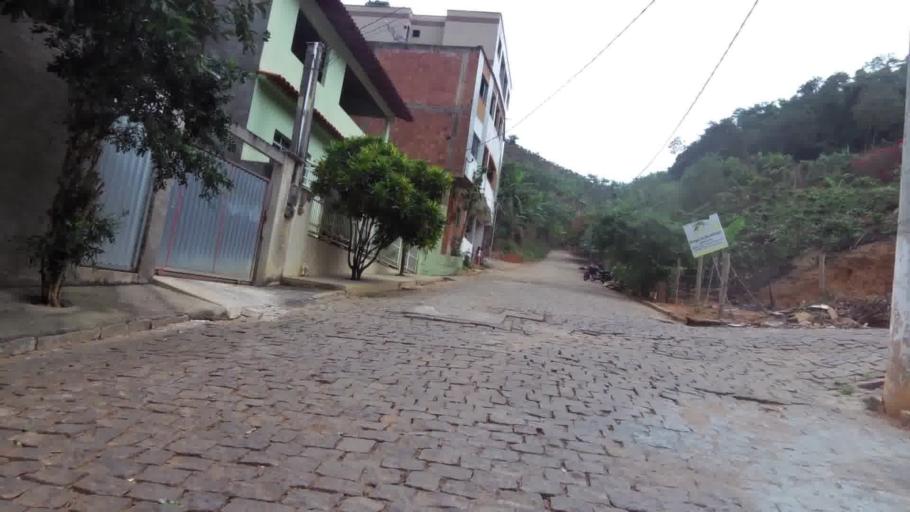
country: BR
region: Espirito Santo
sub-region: Alfredo Chaves
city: Alfredo Chaves
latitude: -20.6377
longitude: -40.7554
